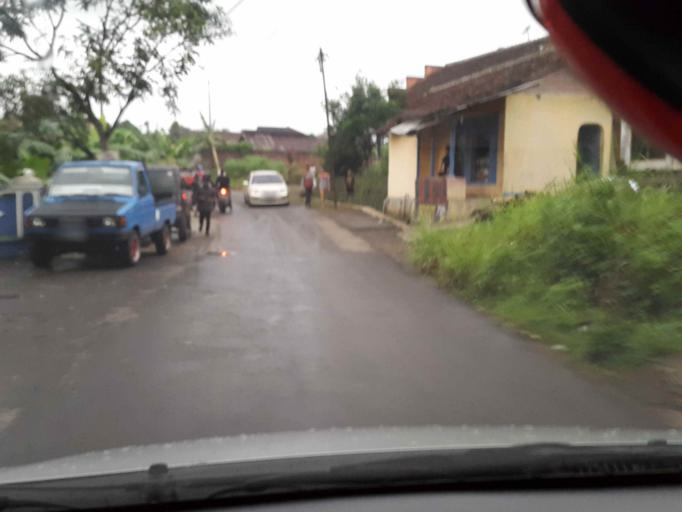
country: ID
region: West Java
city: Sukabumi
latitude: -6.9135
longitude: 106.8744
